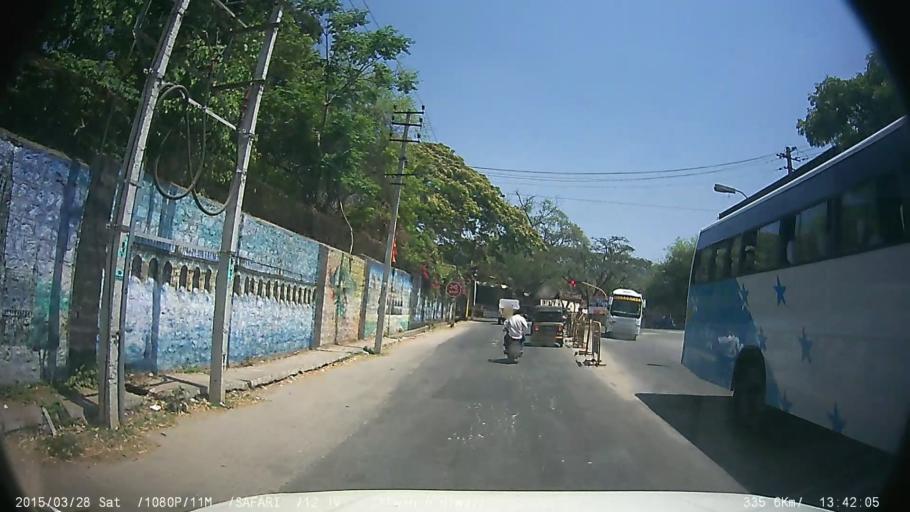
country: IN
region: Karnataka
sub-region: Mysore
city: Mysore
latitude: 12.2988
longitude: 76.6663
